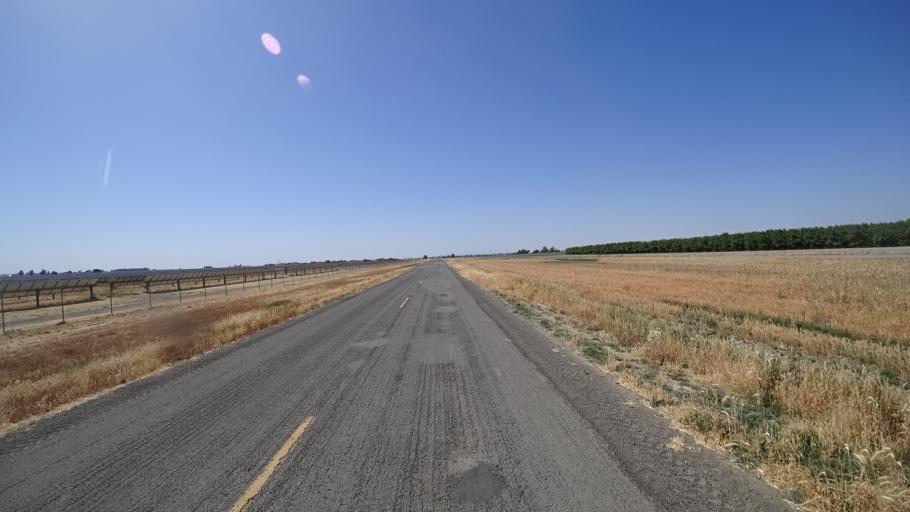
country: US
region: California
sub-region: Kings County
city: Stratford
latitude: 36.2210
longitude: -119.8342
